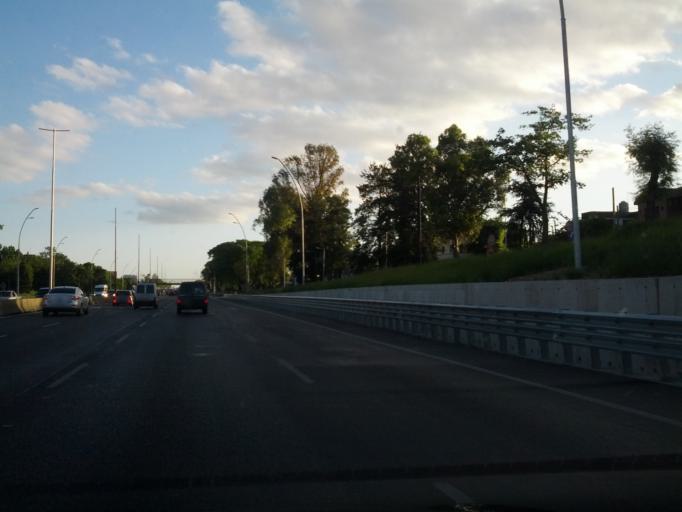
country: AR
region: Buenos Aires
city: Caseros
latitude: -34.6193
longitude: -58.5309
